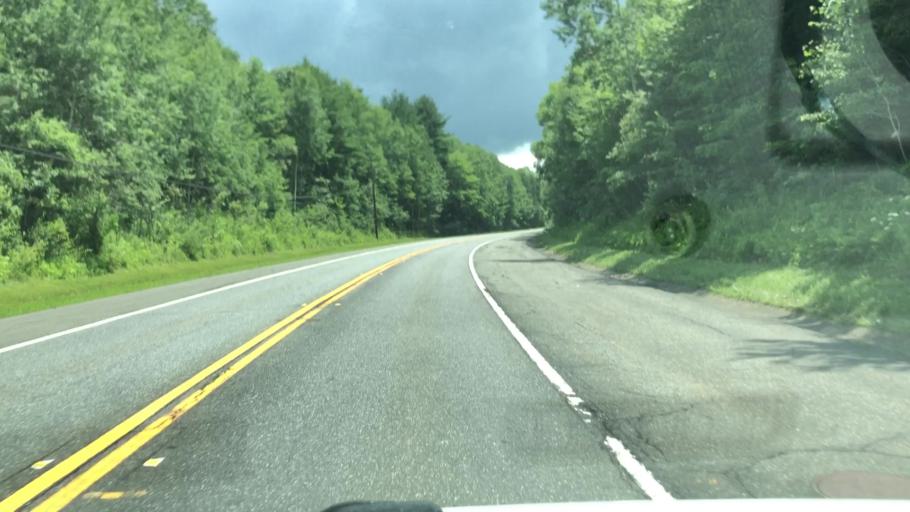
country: US
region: Massachusetts
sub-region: Berkshire County
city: Hinsdale
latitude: 42.4966
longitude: -73.0074
